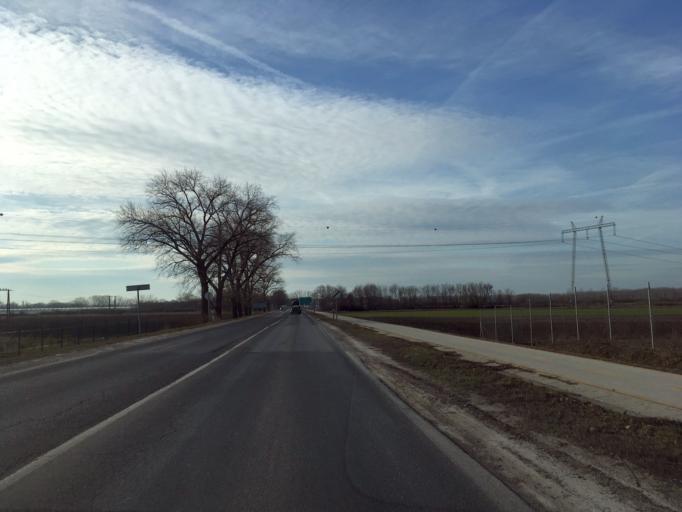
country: HU
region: Gyor-Moson-Sopron
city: Abda
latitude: 47.6802
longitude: 17.5796
